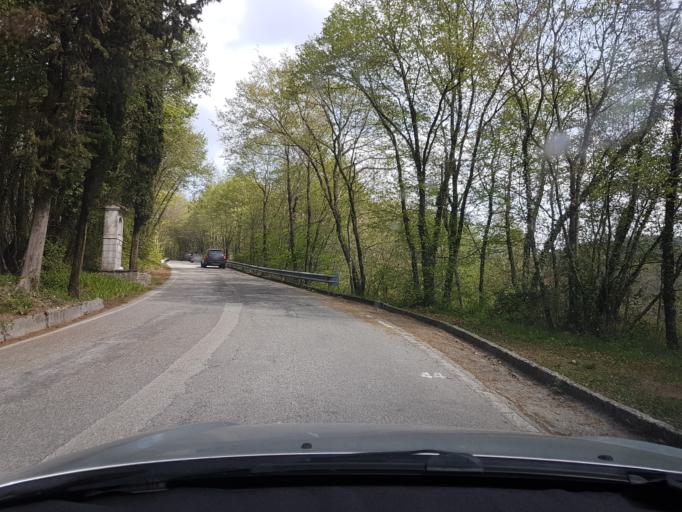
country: IT
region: Friuli Venezia Giulia
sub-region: Provincia di Udine
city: San Pietro al Natisone
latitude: 46.0937
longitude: 13.5071
